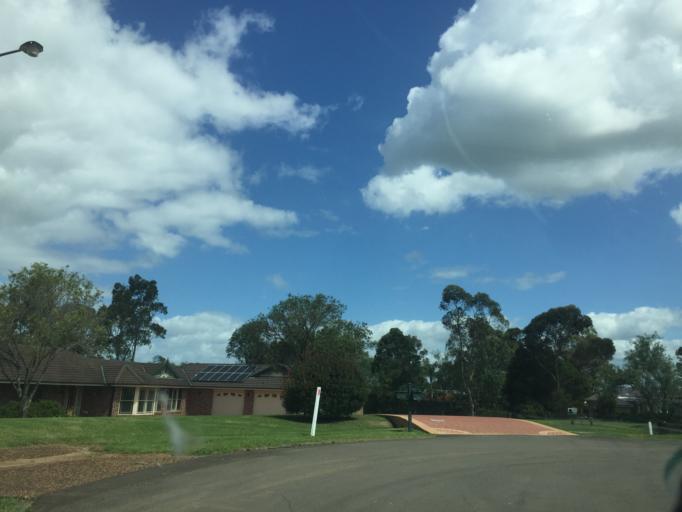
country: AU
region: New South Wales
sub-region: Penrith Municipality
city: Kingswood Park
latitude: -33.7987
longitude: 150.7453
